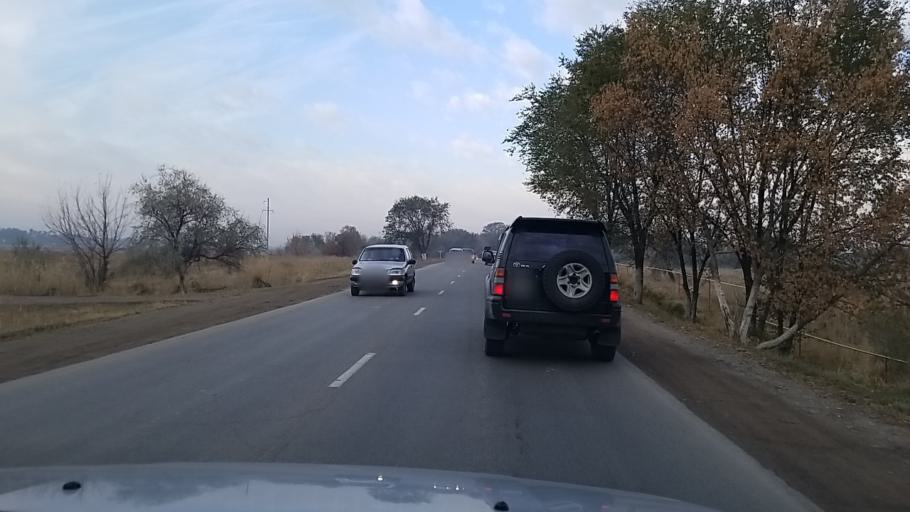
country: KZ
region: Almaty Oblysy
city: Burunday
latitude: 43.3606
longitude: 76.7469
